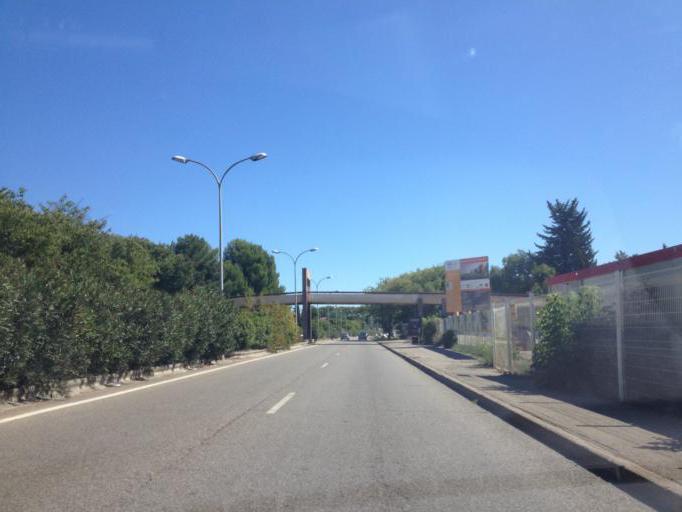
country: FR
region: Provence-Alpes-Cote d'Azur
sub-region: Departement des Bouches-du-Rhone
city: Aix-en-Provence
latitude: 43.5302
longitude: 5.4189
